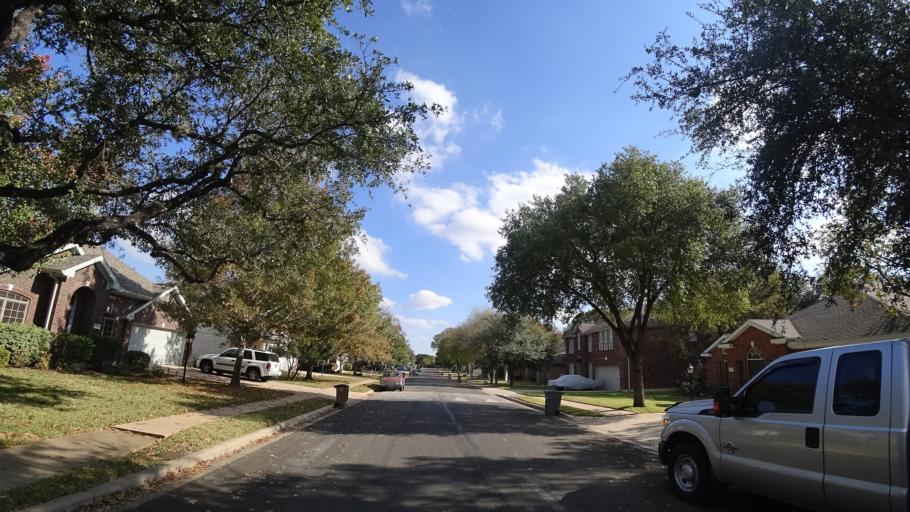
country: US
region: Texas
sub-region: Travis County
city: Shady Hollow
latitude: 30.1824
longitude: -97.8541
